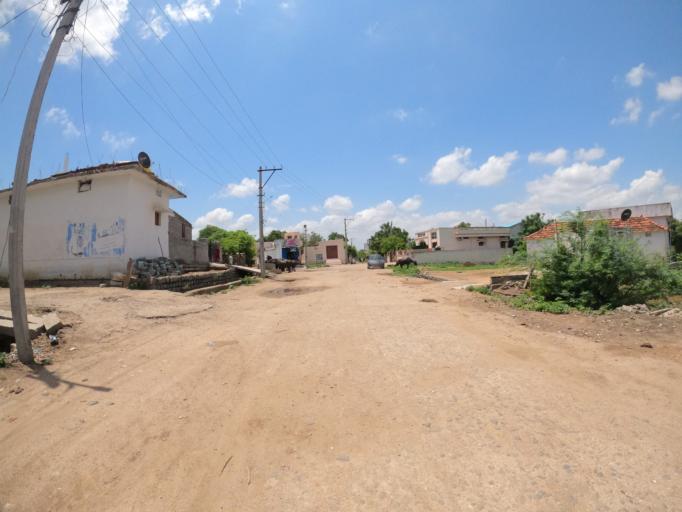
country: IN
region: Telangana
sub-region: Rangareddi
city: Singapur
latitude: 17.4397
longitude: 78.1598
